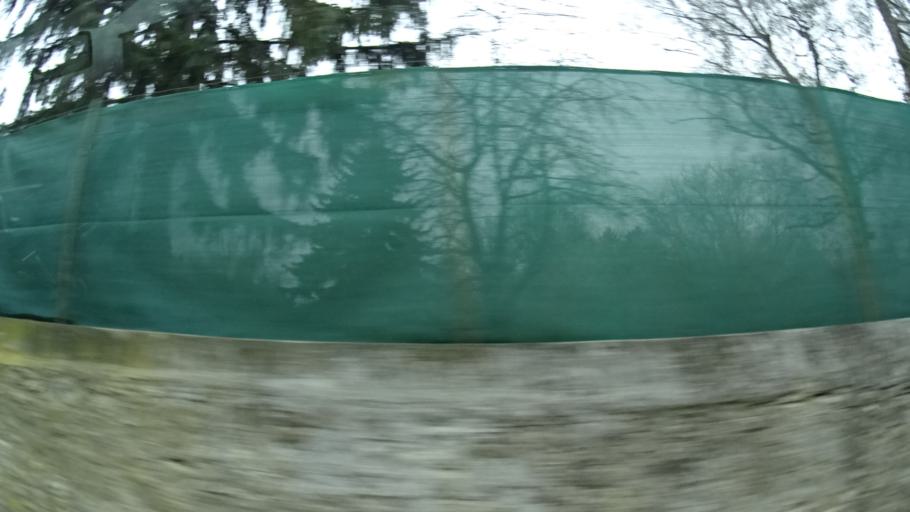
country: DE
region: Bavaria
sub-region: Regierungsbezirk Unterfranken
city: Sulzfeld am Main
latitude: 49.7198
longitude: 10.1474
